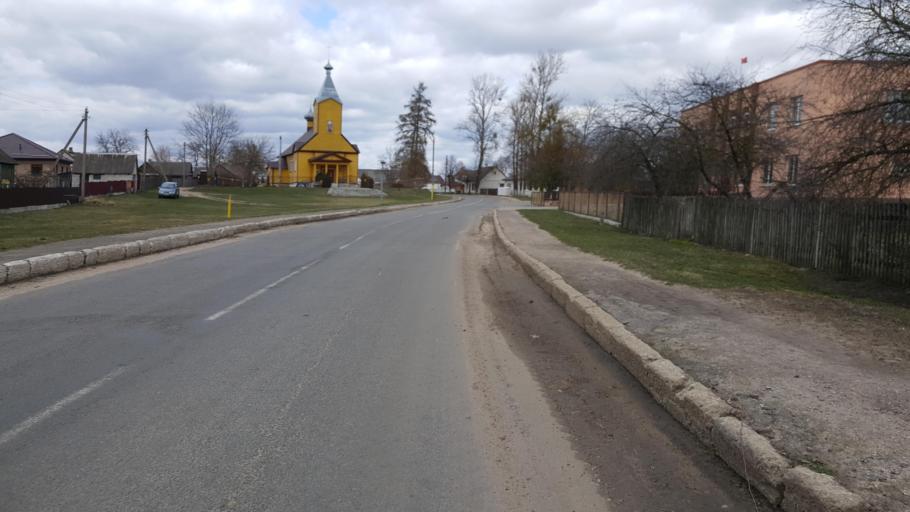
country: PL
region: Podlasie
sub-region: Powiat hajnowski
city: Czeremcha
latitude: 52.4692
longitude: 23.5105
